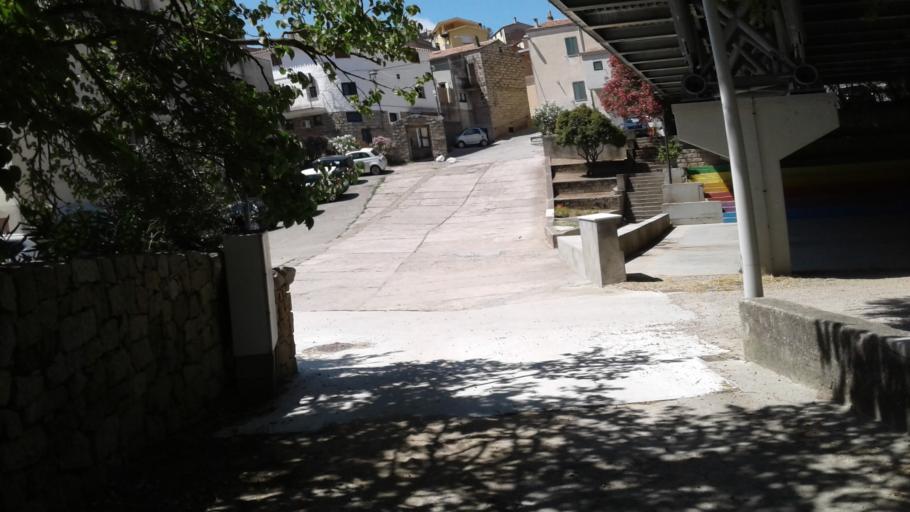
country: IT
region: Sardinia
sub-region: Provincia di Olbia-Tempio
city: Aggius
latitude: 40.9312
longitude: 9.0656
